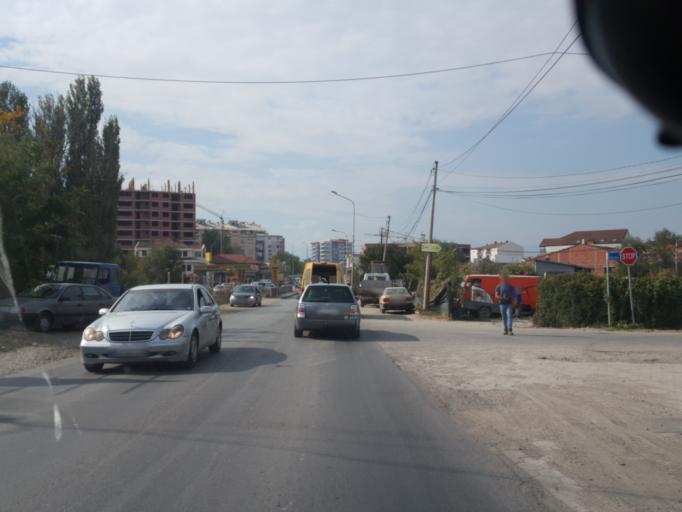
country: XK
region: Gjakova
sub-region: Komuna e Gjakoves
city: Gjakove
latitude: 42.3744
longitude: 20.4451
